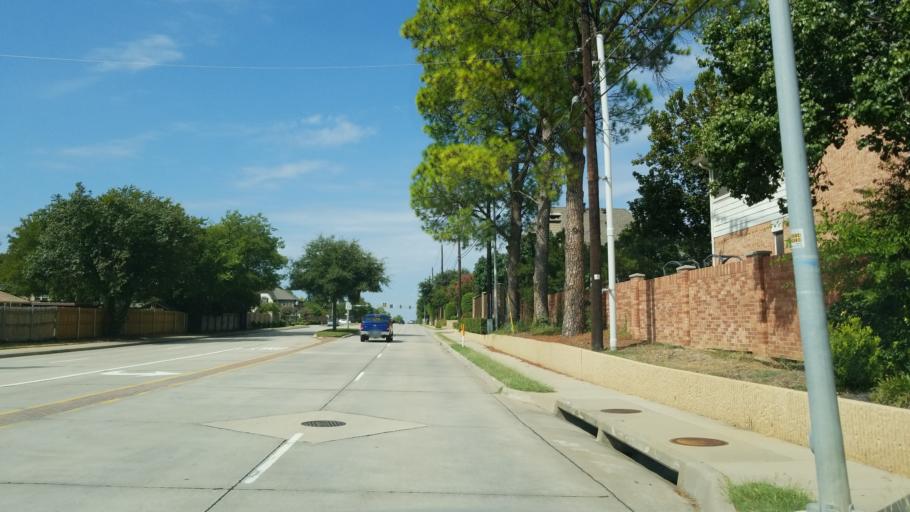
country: US
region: Texas
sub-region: Tarrant County
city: Euless
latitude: 32.8812
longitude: -97.0883
